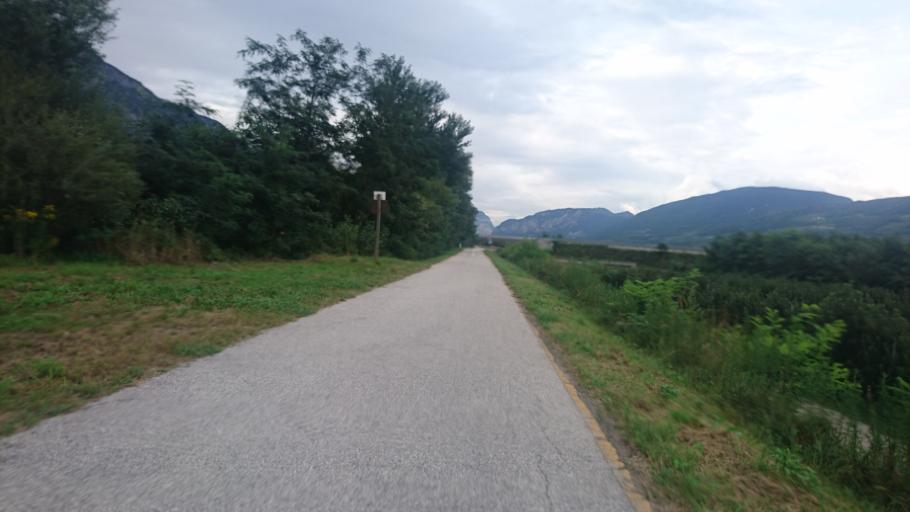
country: IT
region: Trentino-Alto Adige
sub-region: Provincia di Trento
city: Zambana
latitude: 46.1451
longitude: 11.0772
